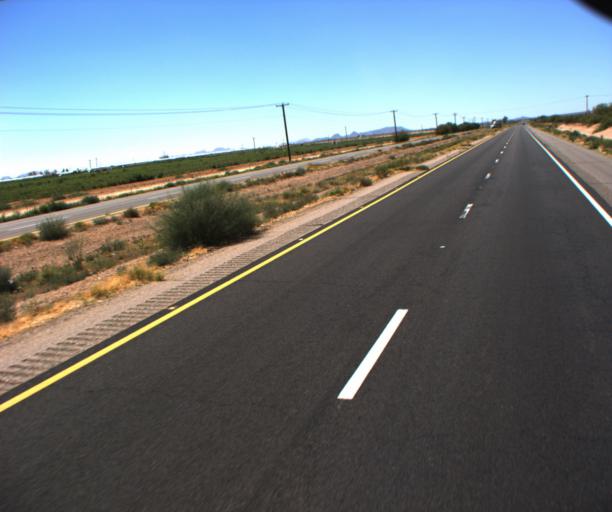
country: US
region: Arizona
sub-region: Pinal County
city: Maricopa
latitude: 32.9189
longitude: -112.0497
